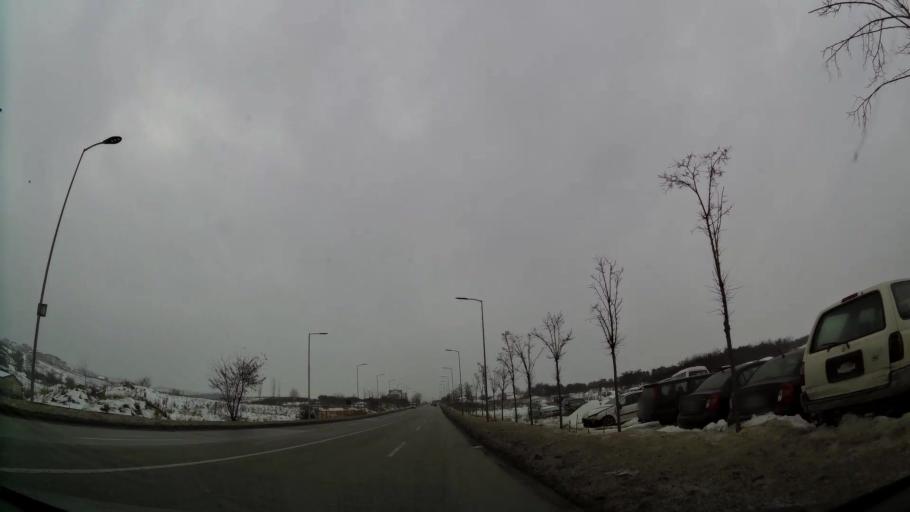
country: XK
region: Pristina
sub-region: Komuna e Prishtines
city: Pristina
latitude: 42.7063
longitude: 21.1548
